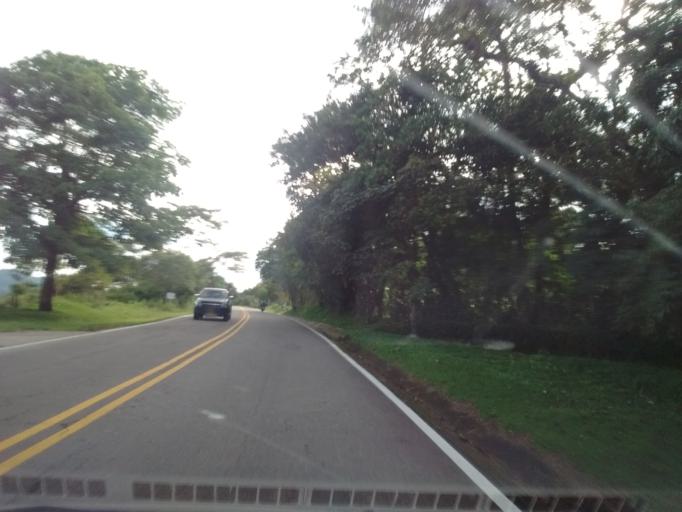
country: CO
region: Huila
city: San Agustin
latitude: 1.8767
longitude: -76.2519
